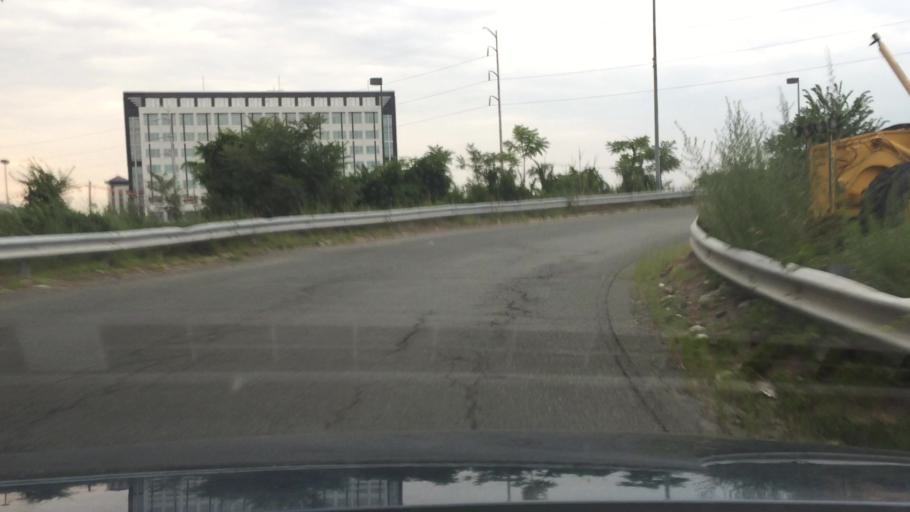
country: US
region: Massachusetts
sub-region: Suffolk County
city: Chelsea
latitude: 42.3952
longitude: -71.0366
